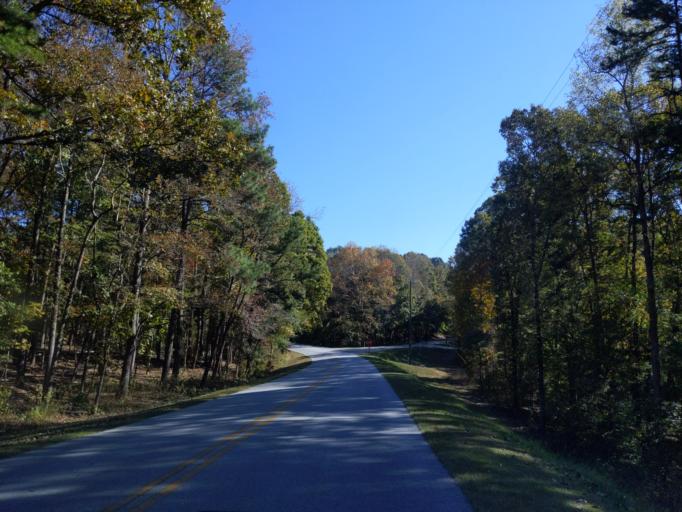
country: US
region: Georgia
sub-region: Franklin County
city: Gumlog
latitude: 34.4949
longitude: -83.0684
